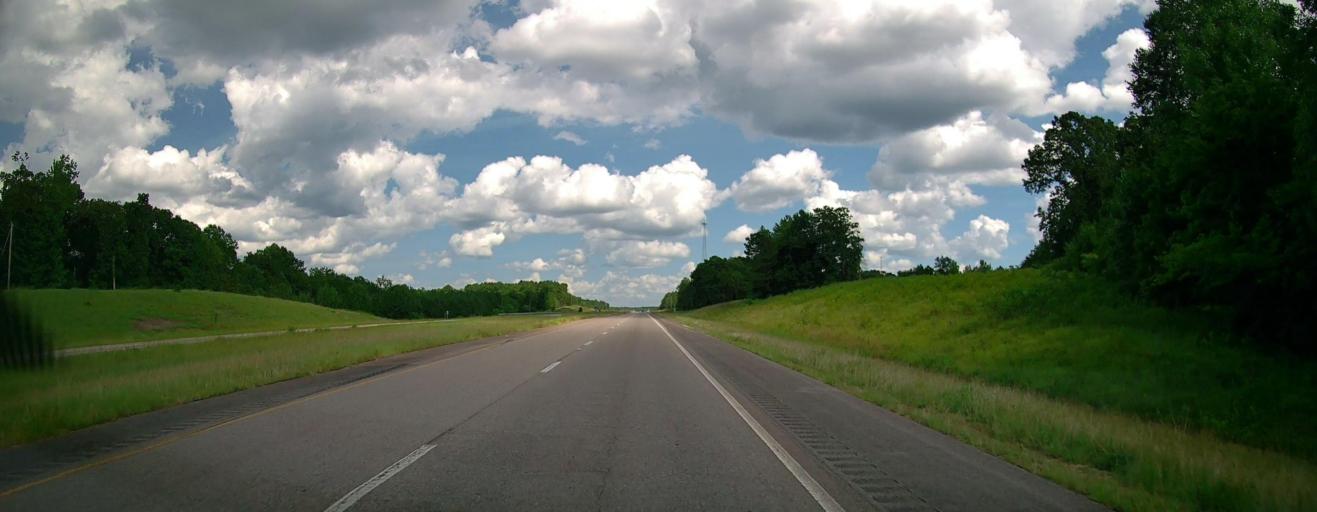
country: US
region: Mississippi
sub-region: Lowndes County
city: New Hope
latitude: 33.4777
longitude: -88.2530
